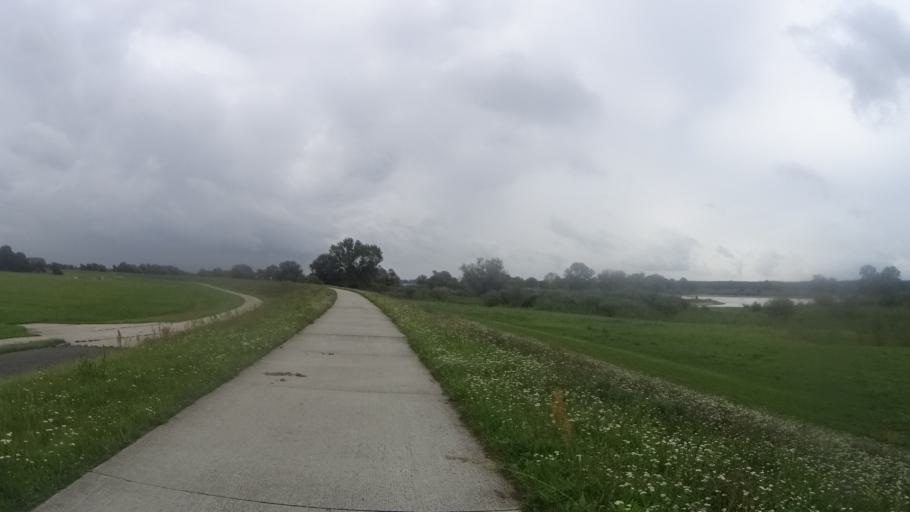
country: DE
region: Lower Saxony
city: Bleckede
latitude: 53.2958
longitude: 10.7642
